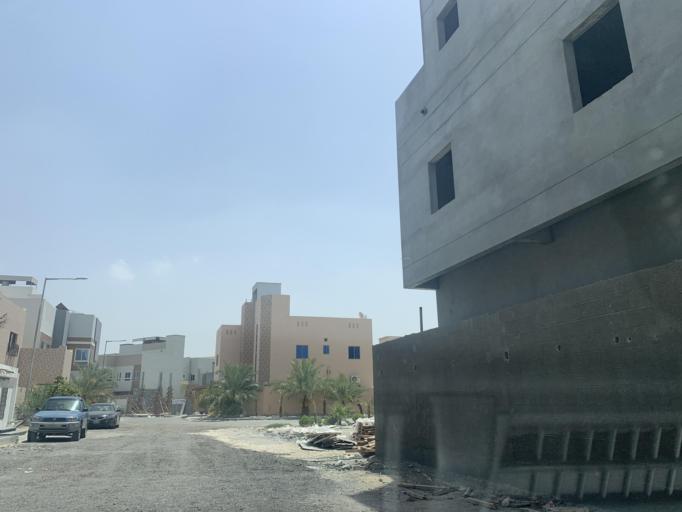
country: BH
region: Central Governorate
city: Madinat Hamad
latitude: 26.1434
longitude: 50.5027
